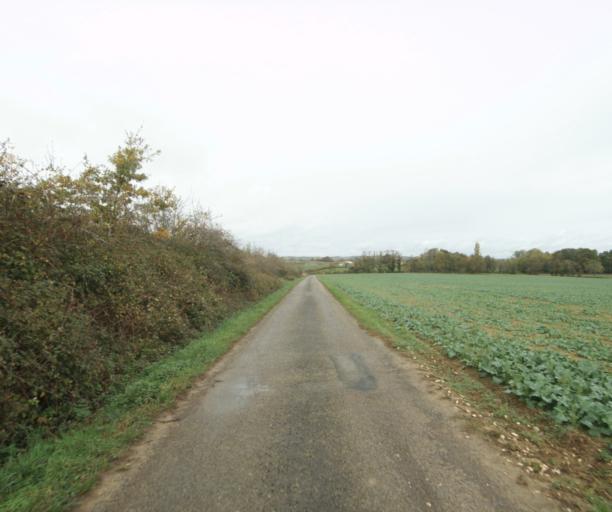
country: FR
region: Rhone-Alpes
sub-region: Departement de l'Ain
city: Pont-de-Vaux
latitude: 46.4573
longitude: 4.8807
